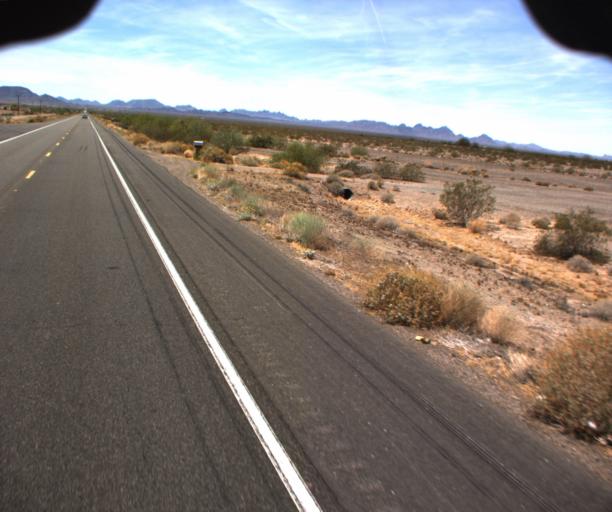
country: US
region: Arizona
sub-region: La Paz County
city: Salome
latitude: 33.7133
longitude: -113.7961
